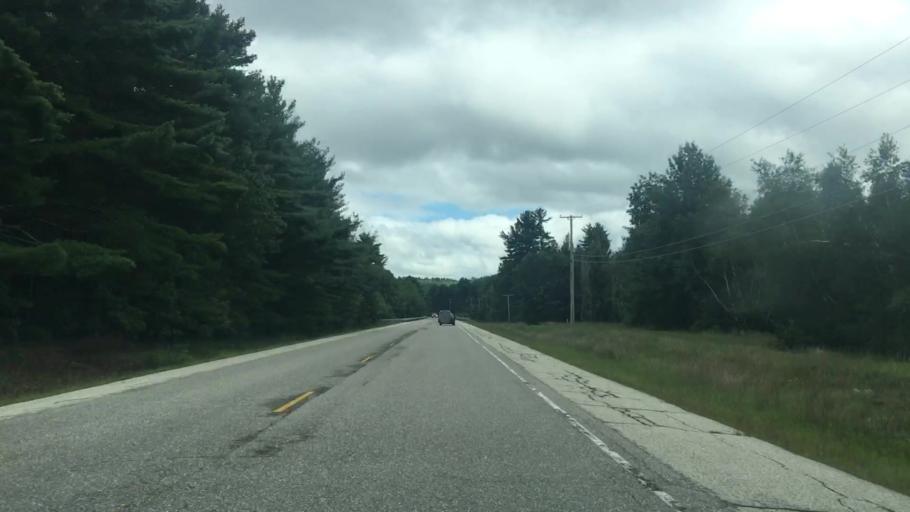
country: US
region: Maine
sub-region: York County
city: Lake Arrowhead
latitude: 43.6275
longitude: -70.7419
